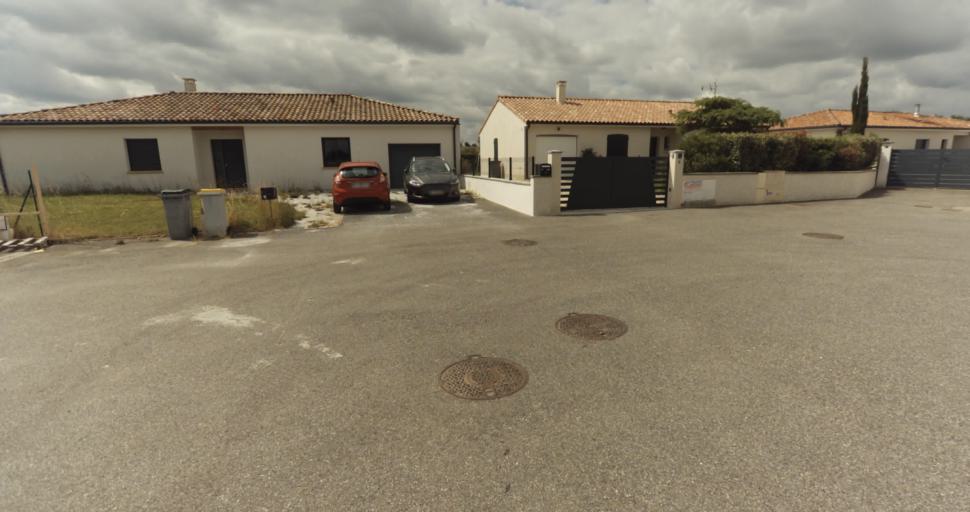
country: FR
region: Midi-Pyrenees
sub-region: Departement de la Haute-Garonne
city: Fontenilles
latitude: 43.5560
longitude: 1.1993
